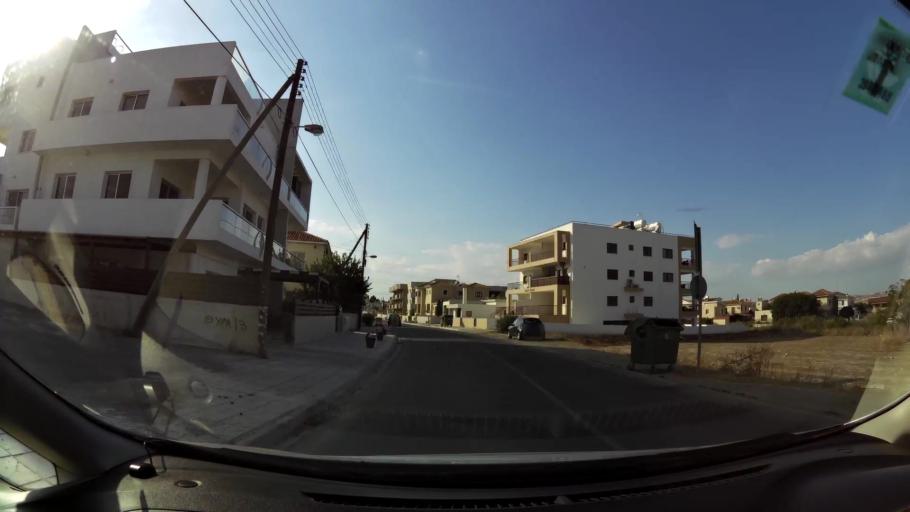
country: CY
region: Larnaka
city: Aradippou
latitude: 34.9422
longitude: 33.6054
